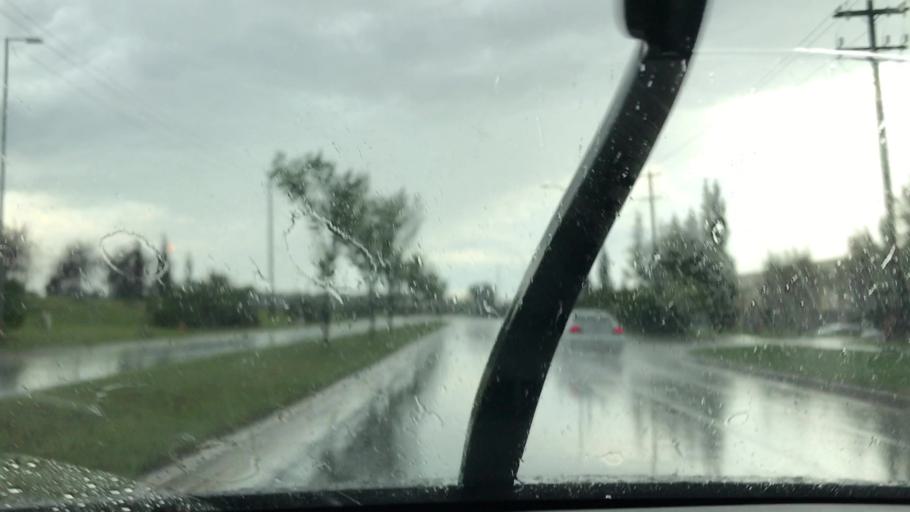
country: CA
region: Alberta
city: Edmonton
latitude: 53.4901
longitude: -113.4481
